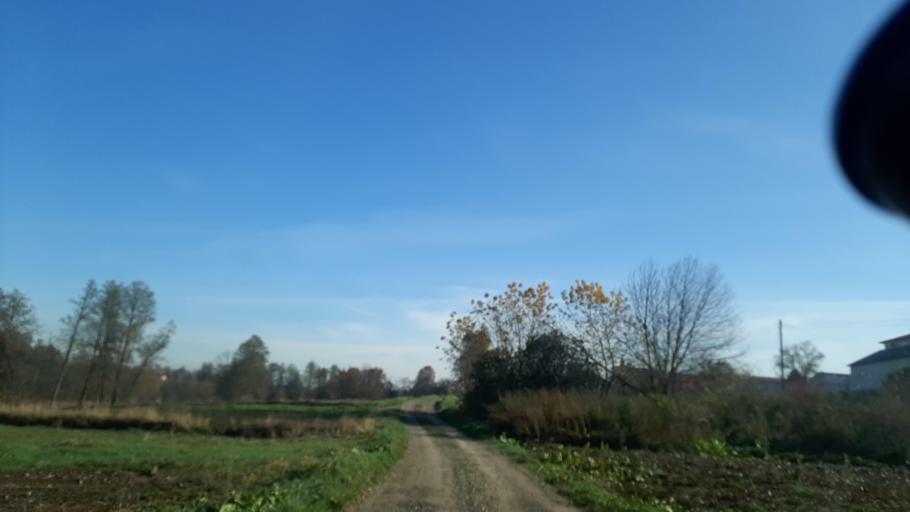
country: PL
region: Lublin Voivodeship
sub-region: Powiat lubelski
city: Lublin
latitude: 51.3114
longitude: 22.5205
